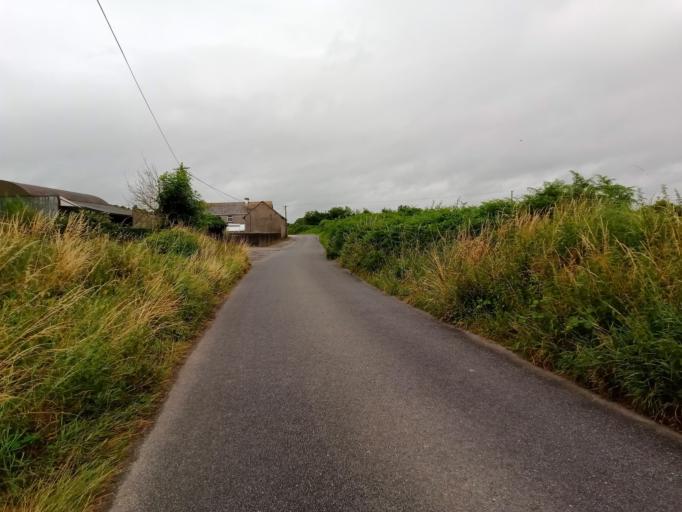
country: IE
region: Leinster
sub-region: Kilkenny
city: Ballyragget
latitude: 52.8112
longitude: -7.4379
